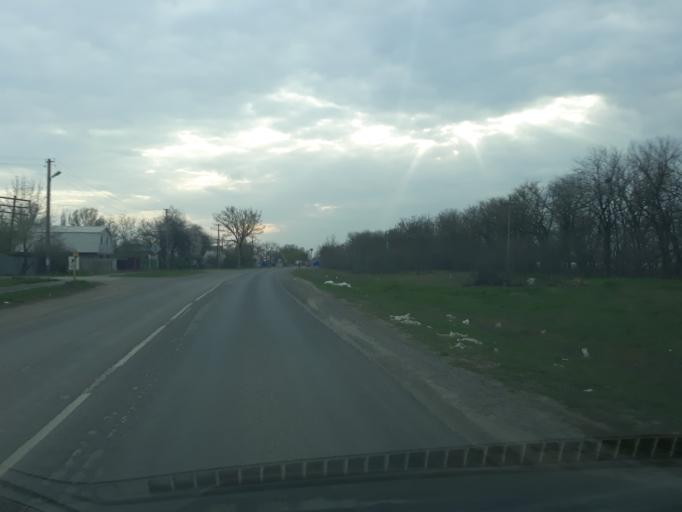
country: RU
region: Rostov
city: Novobessergenovka
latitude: 47.1768
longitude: 38.7803
